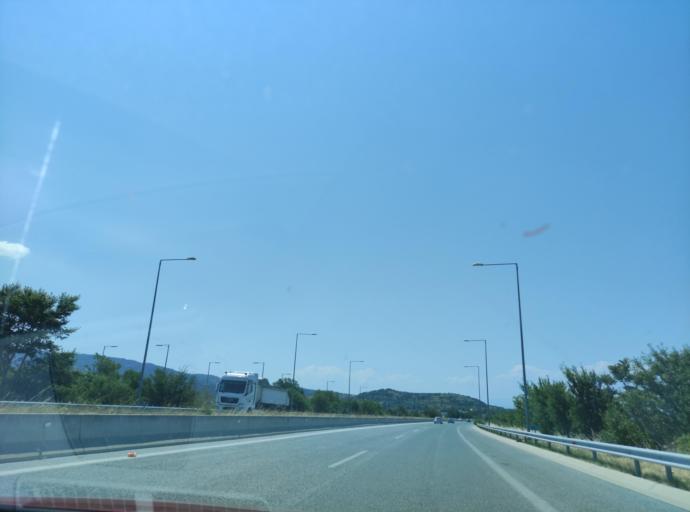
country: GR
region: Central Macedonia
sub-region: Nomos Serron
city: Sidirokastro
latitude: 41.2123
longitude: 23.3886
